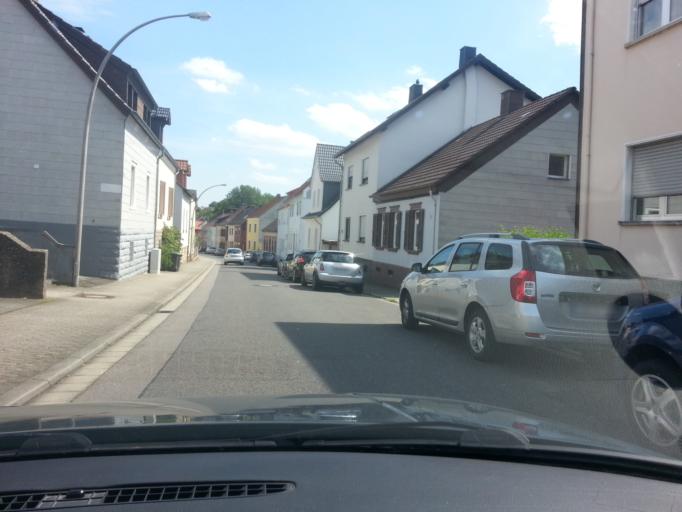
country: DE
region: Saarland
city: Spiesen-Elversberg
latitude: 49.2882
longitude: 7.1586
